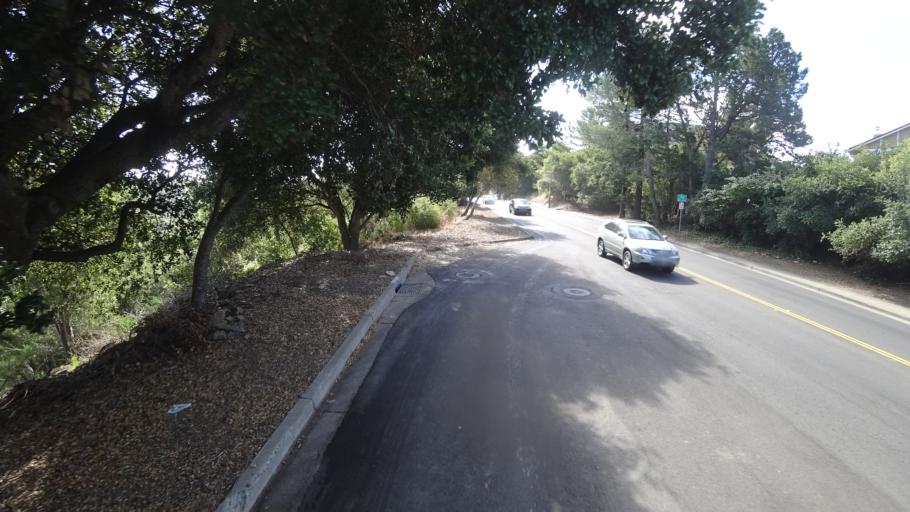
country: US
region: California
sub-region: Alameda County
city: Fairview
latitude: 37.6551
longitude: -122.0325
